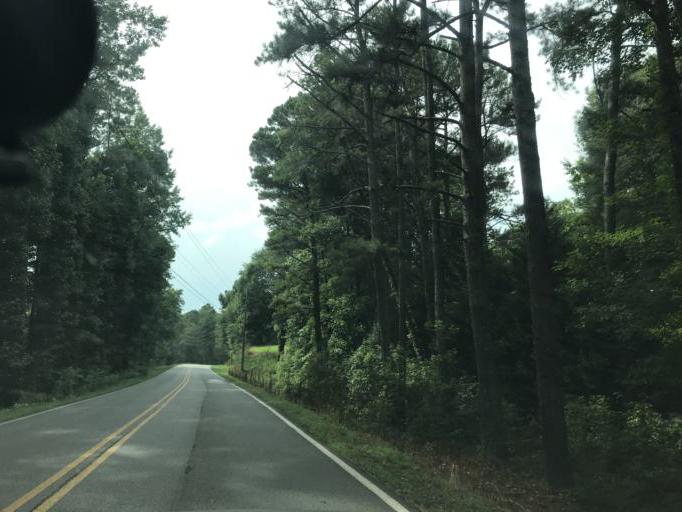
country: US
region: Georgia
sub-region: Forsyth County
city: Cumming
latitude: 34.3053
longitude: -84.1598
